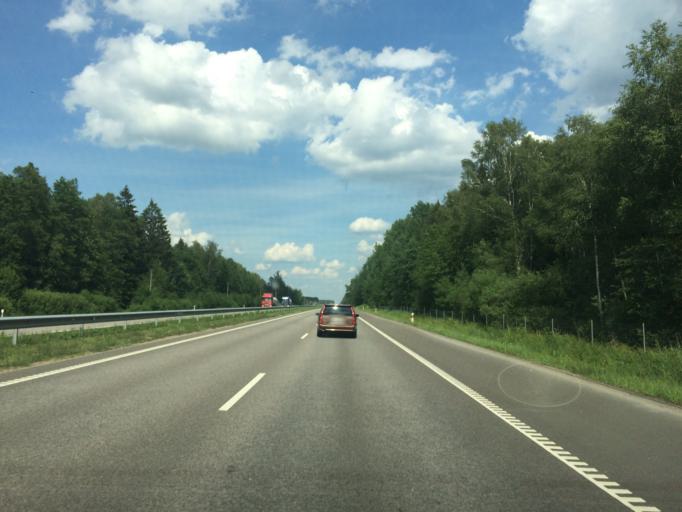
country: LT
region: Kauno apskritis
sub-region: Kauno rajonas
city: Karmelava
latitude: 55.0182
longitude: 24.1733
